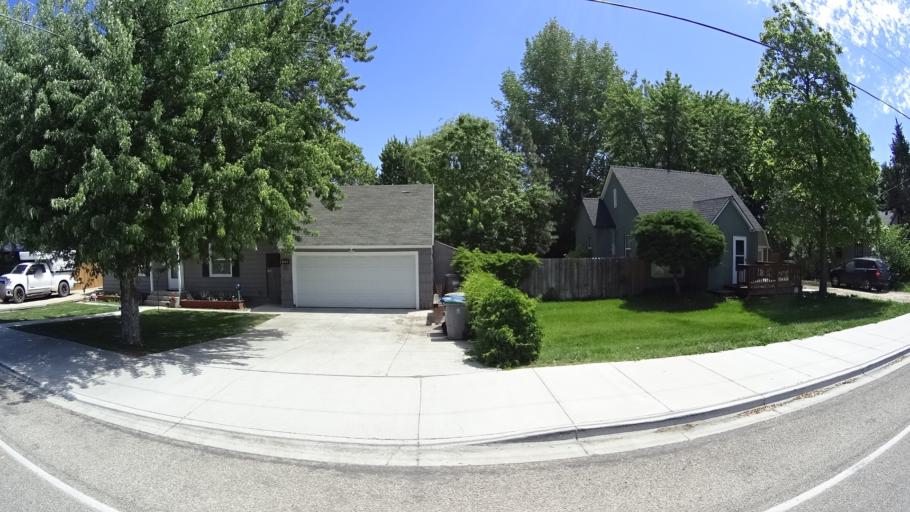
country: US
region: Idaho
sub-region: Ada County
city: Garden City
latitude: 43.5925
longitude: -116.2336
